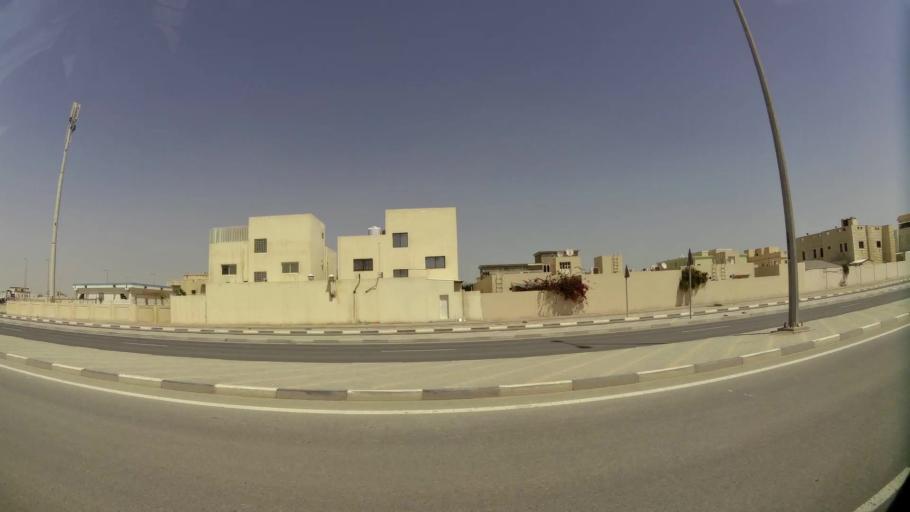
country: QA
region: Baladiyat Umm Salal
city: Umm Salal Muhammad
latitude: 25.3842
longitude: 51.4550
